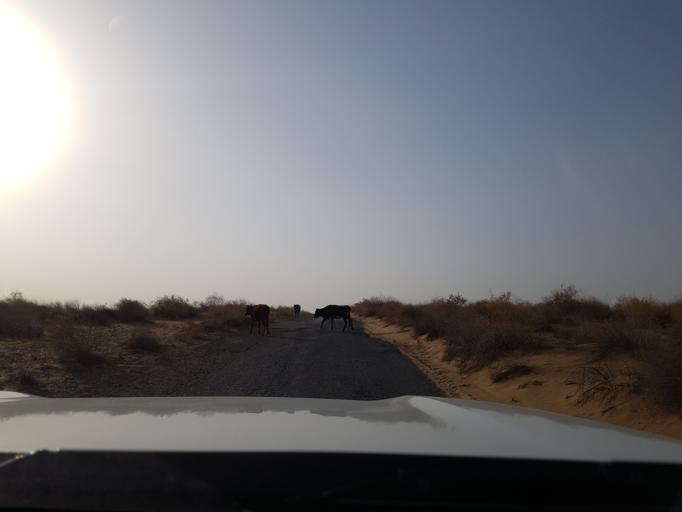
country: UZ
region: Xorazm
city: Hazorasp
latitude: 41.1967
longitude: 60.9373
